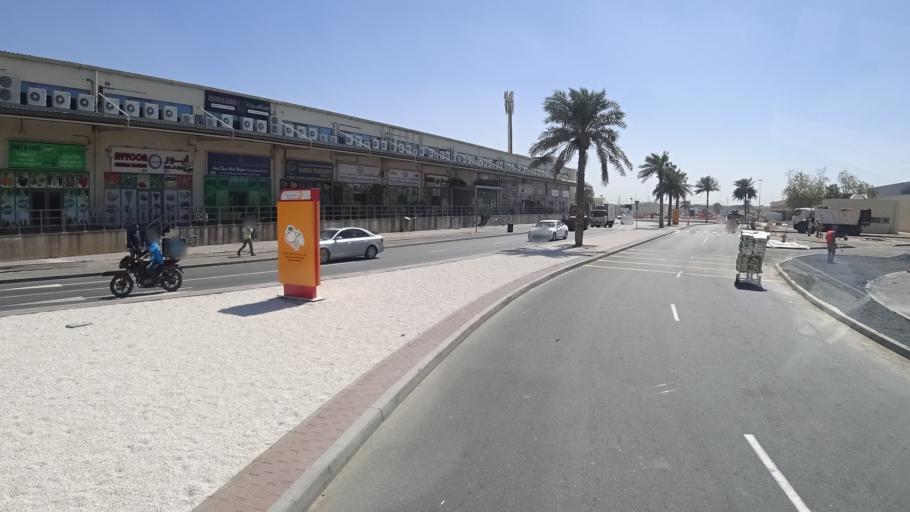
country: AE
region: Ash Shariqah
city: Sharjah
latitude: 25.1753
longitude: 55.3929
